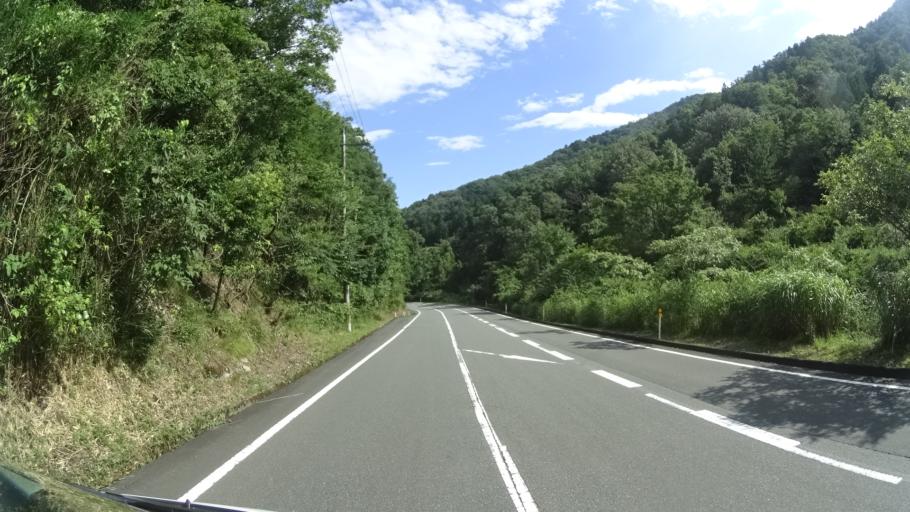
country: JP
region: Kyoto
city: Fukuchiyama
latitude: 35.3439
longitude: 135.1591
